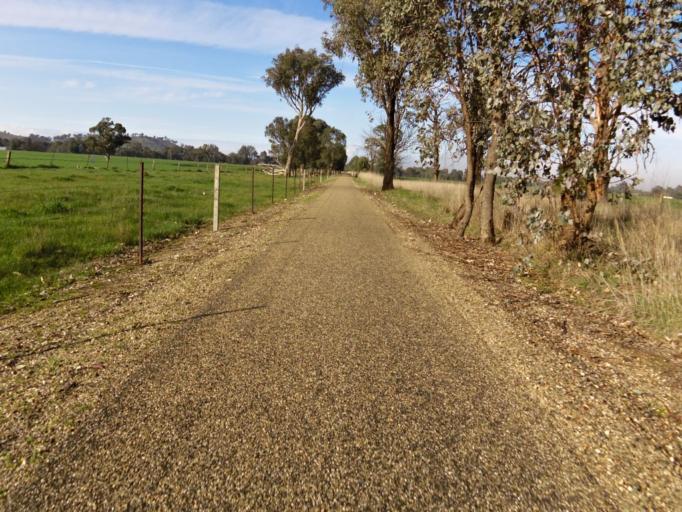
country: AU
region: Victoria
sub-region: Wangaratta
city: Wangaratta
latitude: -36.4225
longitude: 146.5503
